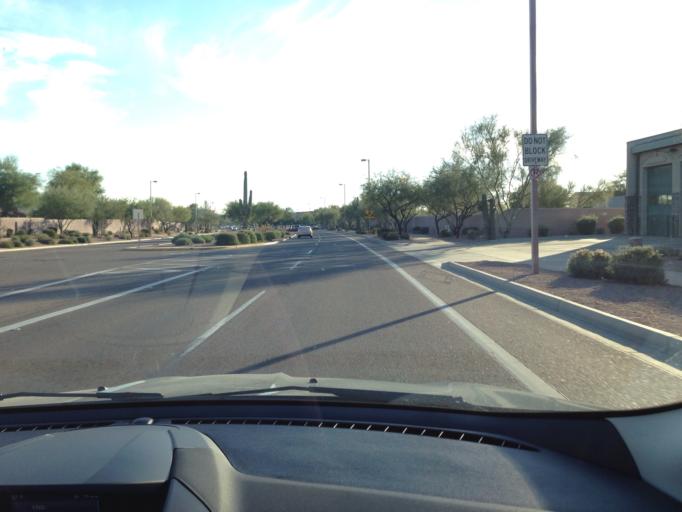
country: US
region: Arizona
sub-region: Maricopa County
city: Carefree
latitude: 33.6832
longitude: -111.9764
